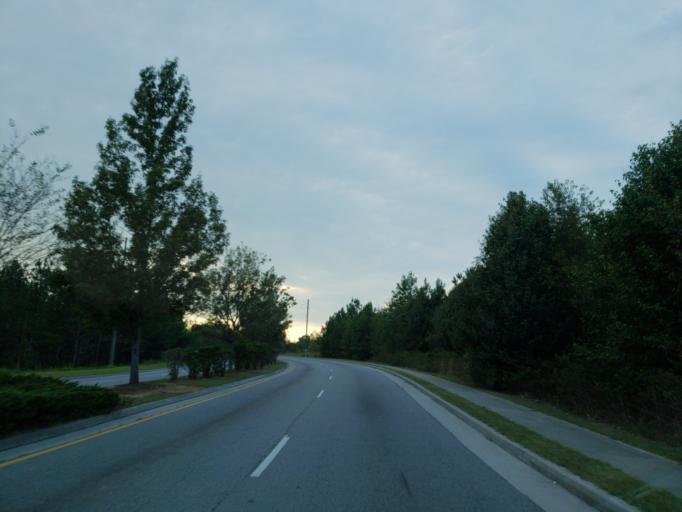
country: US
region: Georgia
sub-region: Cobb County
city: Powder Springs
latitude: 33.8670
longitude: -84.6870
